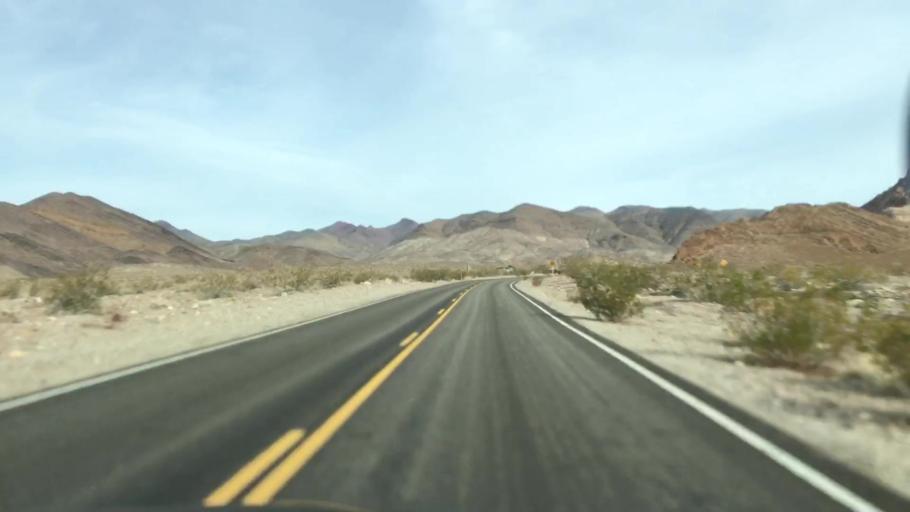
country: US
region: Nevada
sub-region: Nye County
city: Beatty
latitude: 36.7215
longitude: -116.9790
